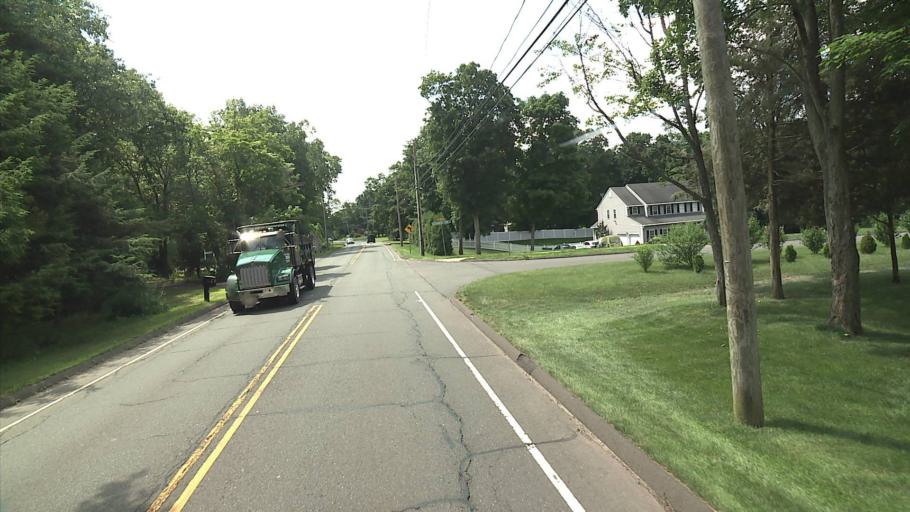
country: US
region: Connecticut
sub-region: Middlesex County
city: Cromwell
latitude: 41.6367
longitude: -72.6052
